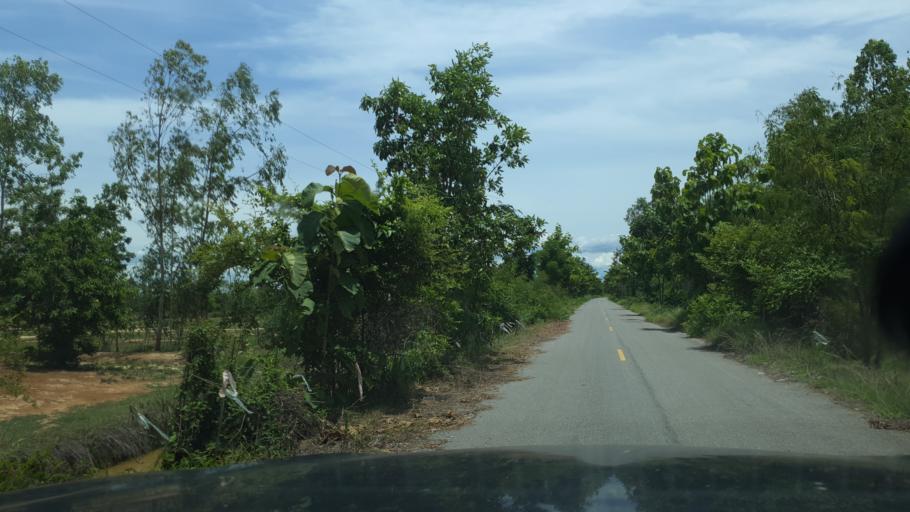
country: TH
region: Sukhothai
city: Ban Na
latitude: 17.1124
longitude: 99.6775
